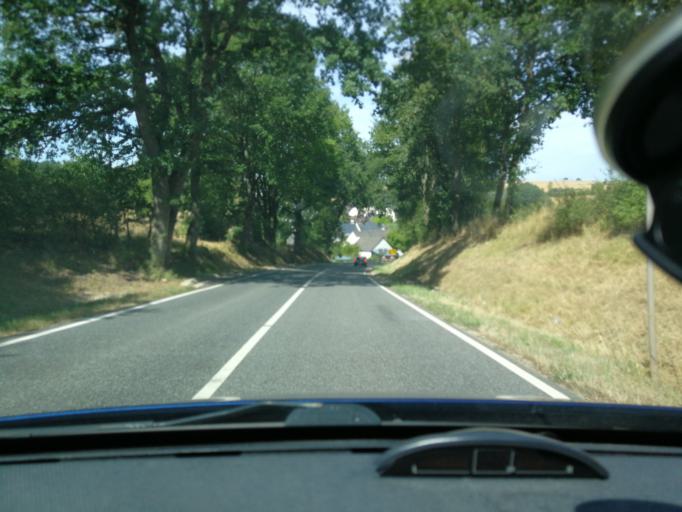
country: DE
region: Rheinland-Pfalz
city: Arenrath
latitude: 49.9506
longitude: 6.7422
